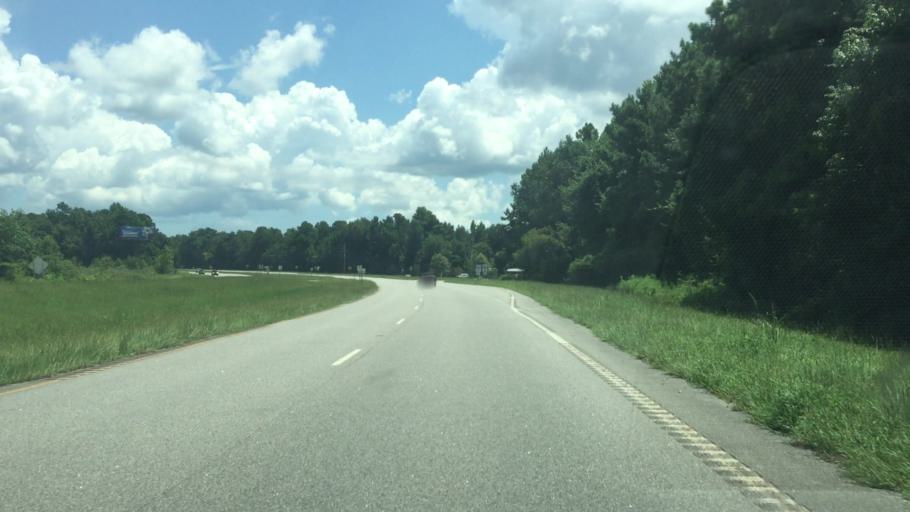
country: US
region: South Carolina
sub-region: Horry County
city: Loris
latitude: 34.0195
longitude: -78.7949
